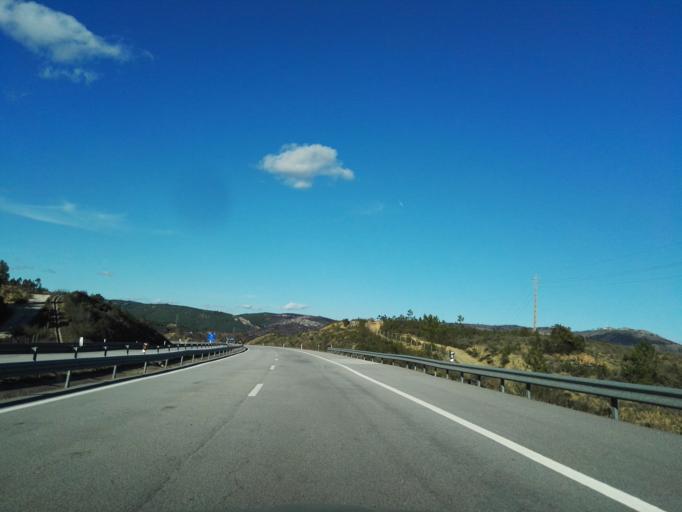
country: PT
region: Portalegre
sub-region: Nisa
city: Nisa
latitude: 39.6540
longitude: -7.7389
